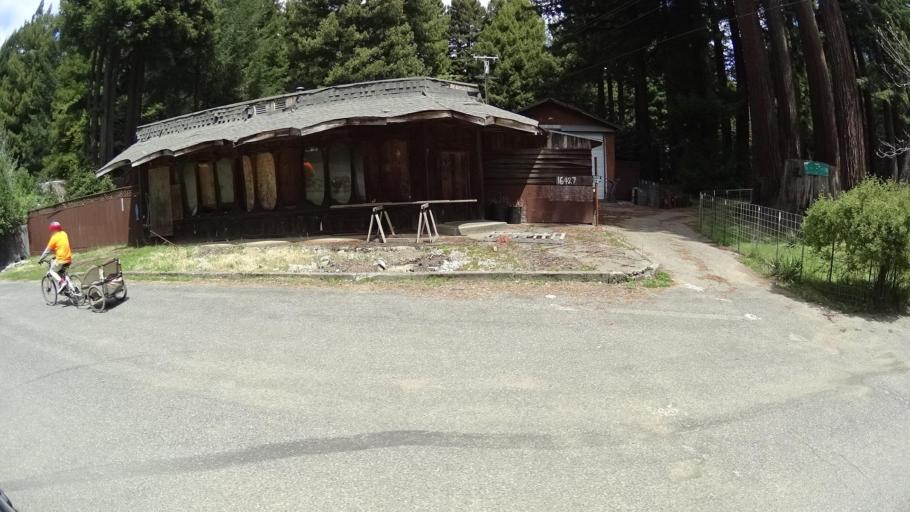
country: US
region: California
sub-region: Humboldt County
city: Redway
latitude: 40.0236
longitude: -123.9427
